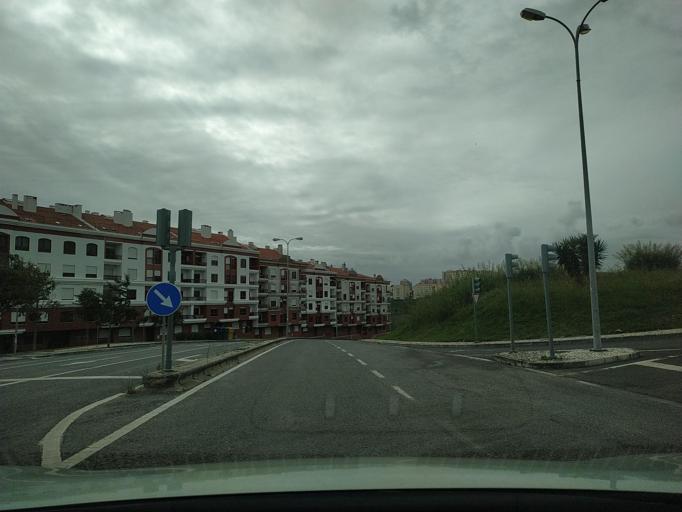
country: PT
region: Lisbon
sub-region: Sintra
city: Queluz
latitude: 38.7633
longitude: -9.2445
